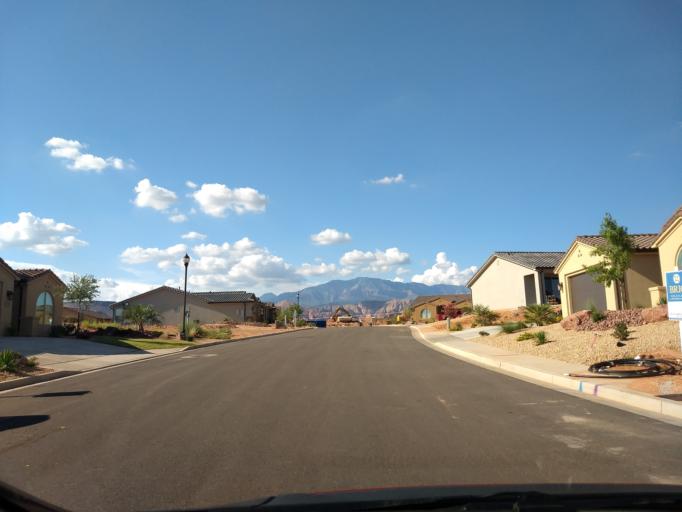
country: US
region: Utah
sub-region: Washington County
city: Washington
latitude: 37.1440
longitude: -113.5162
